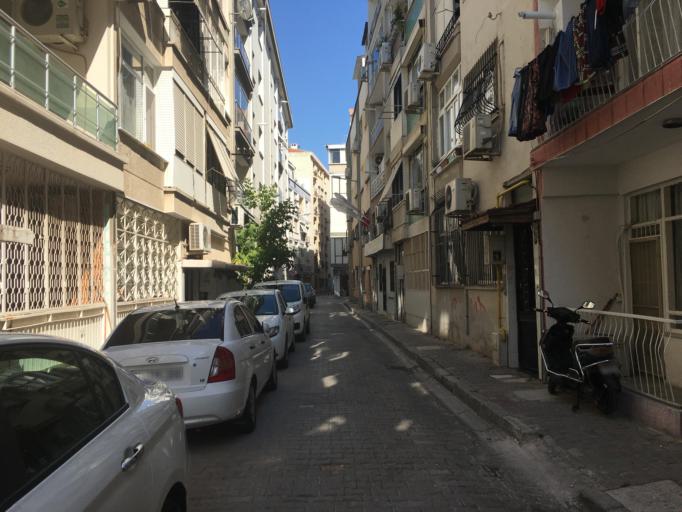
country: TR
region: Izmir
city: Karsiyaka
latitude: 38.4584
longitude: 27.1241
